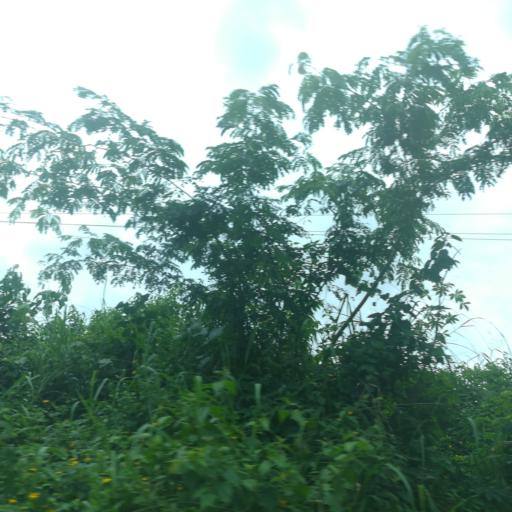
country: NG
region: Ogun
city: Odogbolu
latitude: 6.6584
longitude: 3.7117
